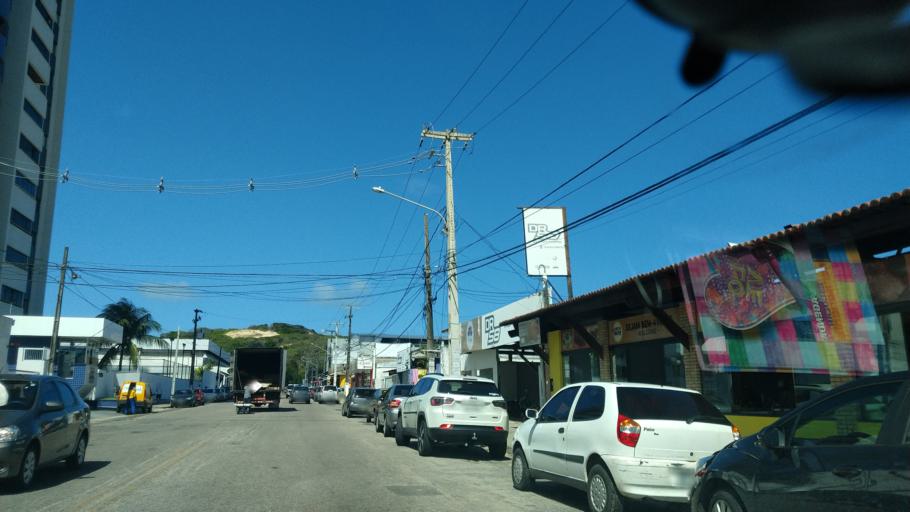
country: BR
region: Rio Grande do Norte
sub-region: Natal
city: Natal
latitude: -5.8681
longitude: -35.1862
